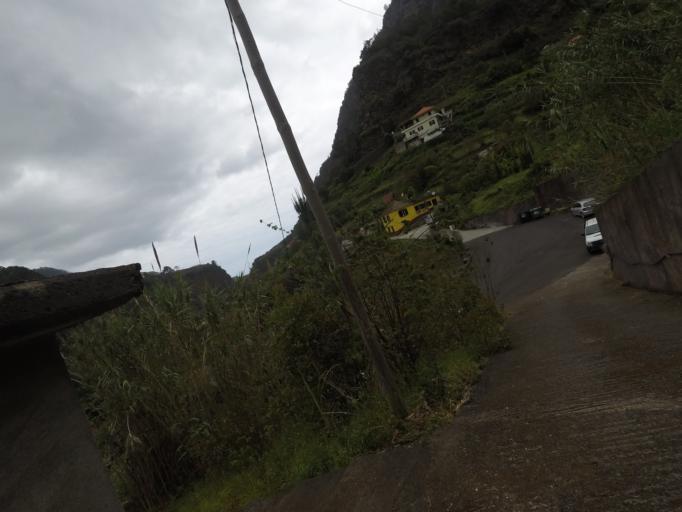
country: PT
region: Madeira
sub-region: Santana
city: Santana
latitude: 32.7735
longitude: -16.8467
